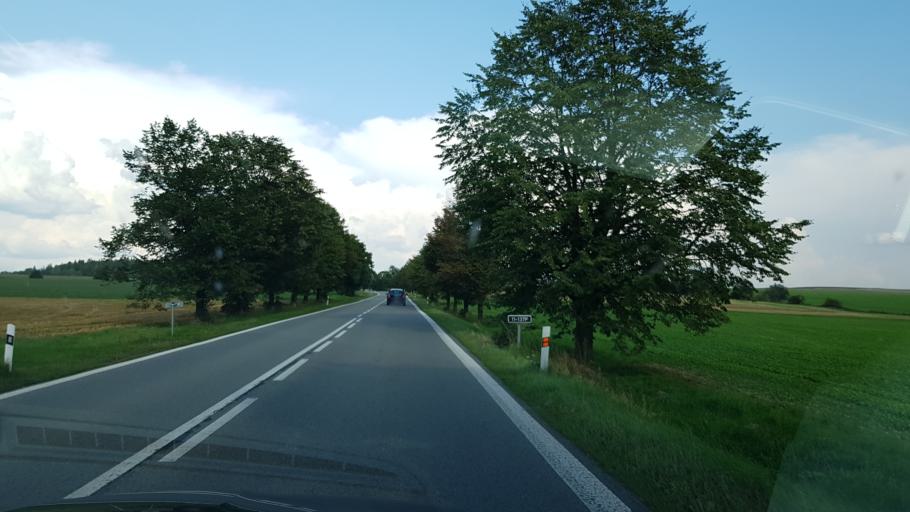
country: CZ
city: Vamberk
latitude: 50.1069
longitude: 16.3725
